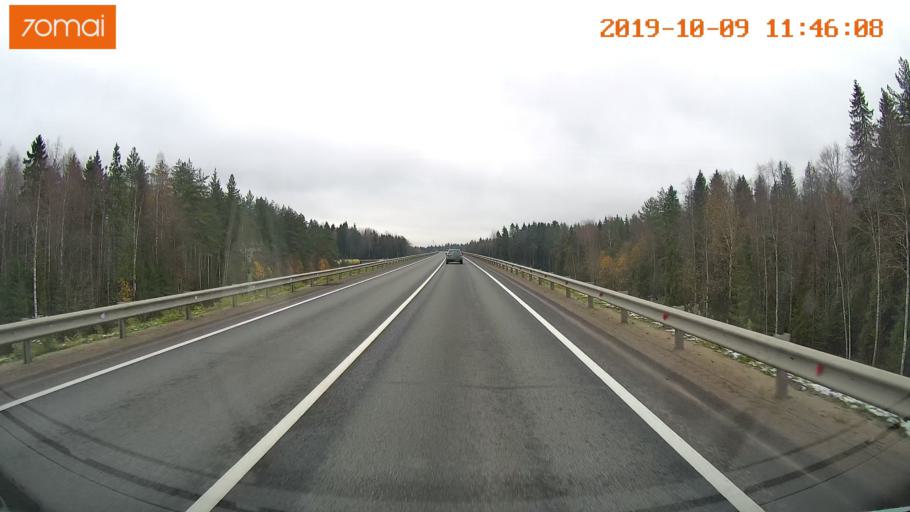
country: RU
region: Vologda
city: Gryazovets
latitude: 58.8586
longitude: 40.1996
